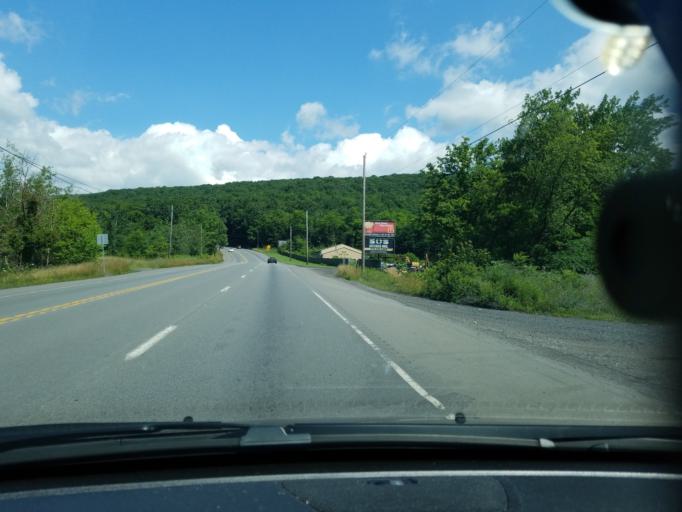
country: US
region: Pennsylvania
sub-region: Northumberland County
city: Mount Carmel
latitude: 40.8043
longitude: -76.4400
